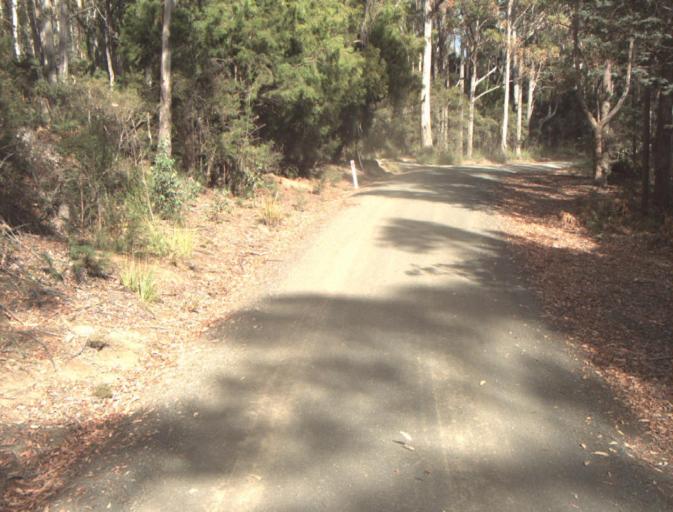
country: AU
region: Tasmania
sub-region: Launceston
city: Mayfield
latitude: -41.2647
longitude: 147.2316
